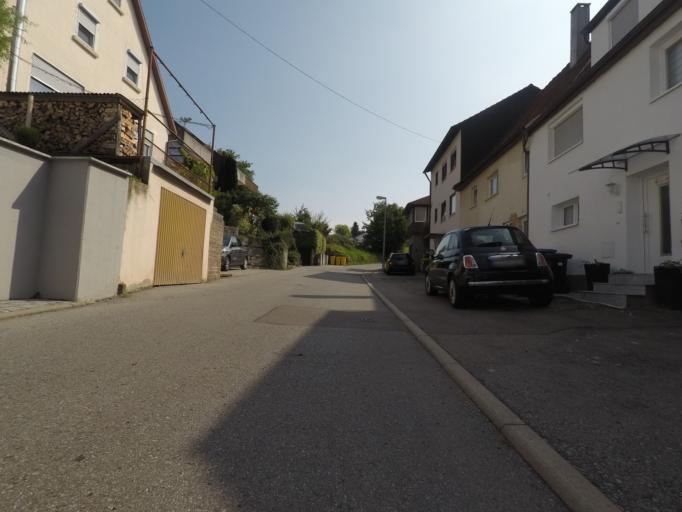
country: DE
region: Baden-Wuerttemberg
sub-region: Regierungsbezirk Stuttgart
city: Winterbach
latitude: 48.7957
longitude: 9.5032
